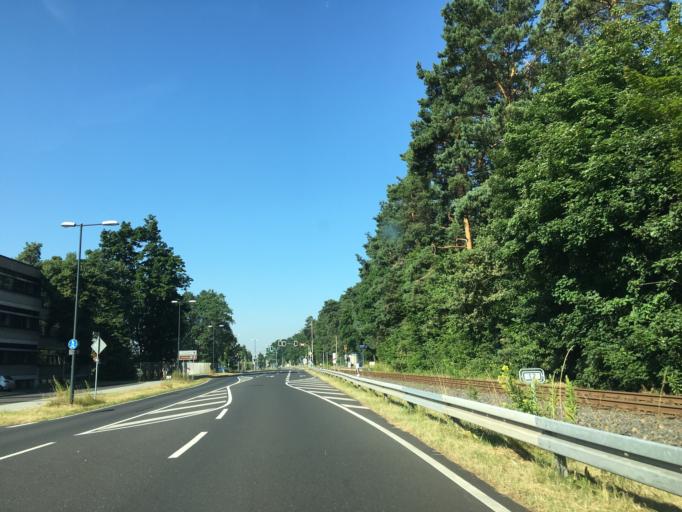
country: DE
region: Bavaria
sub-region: Regierungsbezirk Unterfranken
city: Kahl am Main
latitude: 50.0797
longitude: 9.0170
